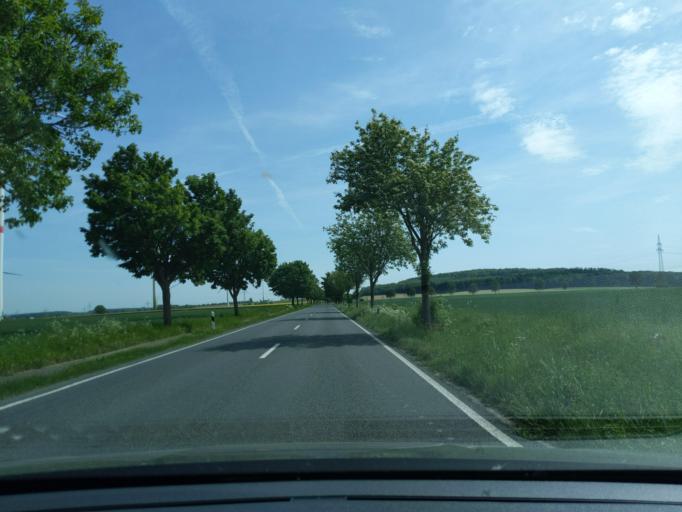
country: DE
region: Lower Saxony
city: Ronnenberg
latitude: 52.2141
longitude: 9.6602
